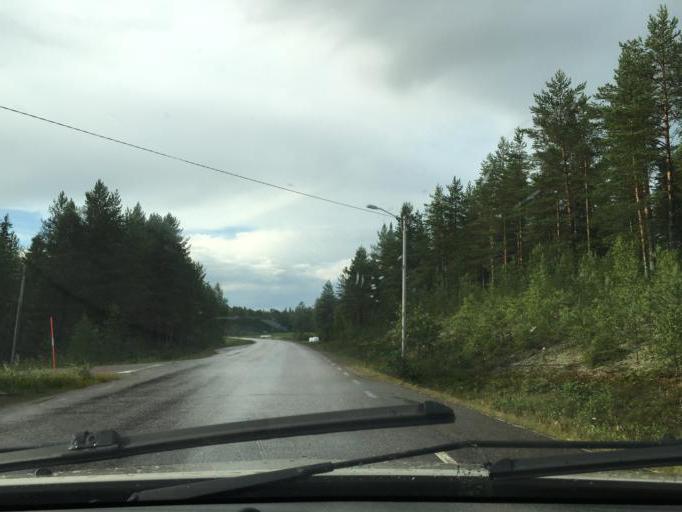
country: SE
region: Norrbotten
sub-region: Kalix Kommun
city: Rolfs
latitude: 65.9397
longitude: 22.8927
